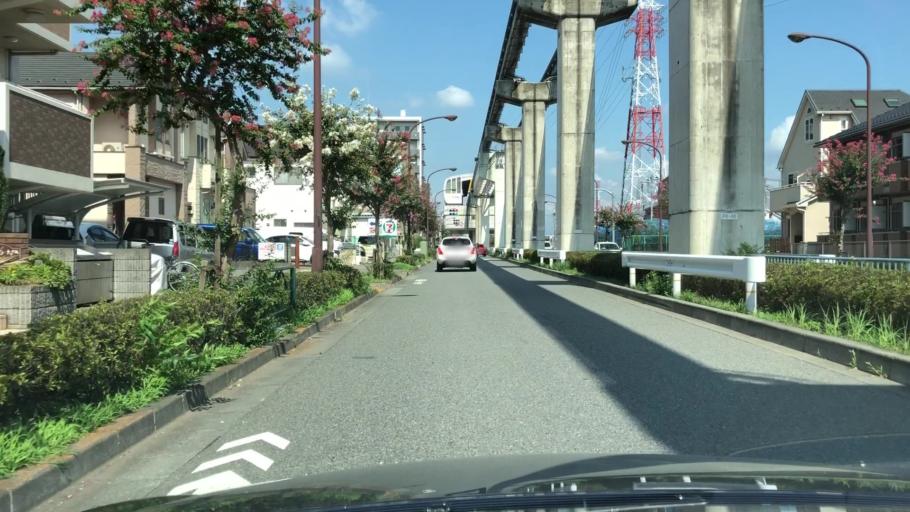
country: JP
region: Tokyo
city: Hino
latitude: 35.6769
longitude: 139.4114
